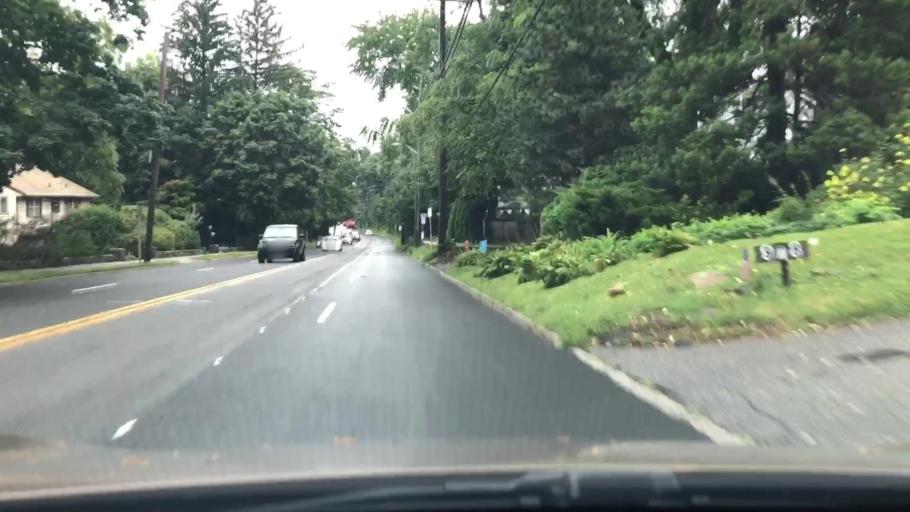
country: US
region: New York
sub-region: Westchester County
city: Greenville
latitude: 40.9855
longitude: -73.7979
